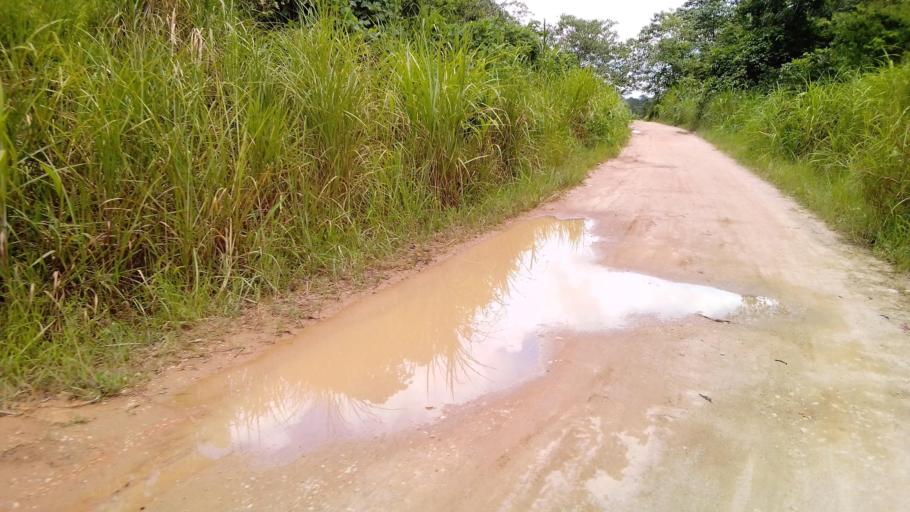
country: SL
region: Eastern Province
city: Koidu
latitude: 8.6816
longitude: -10.9665
